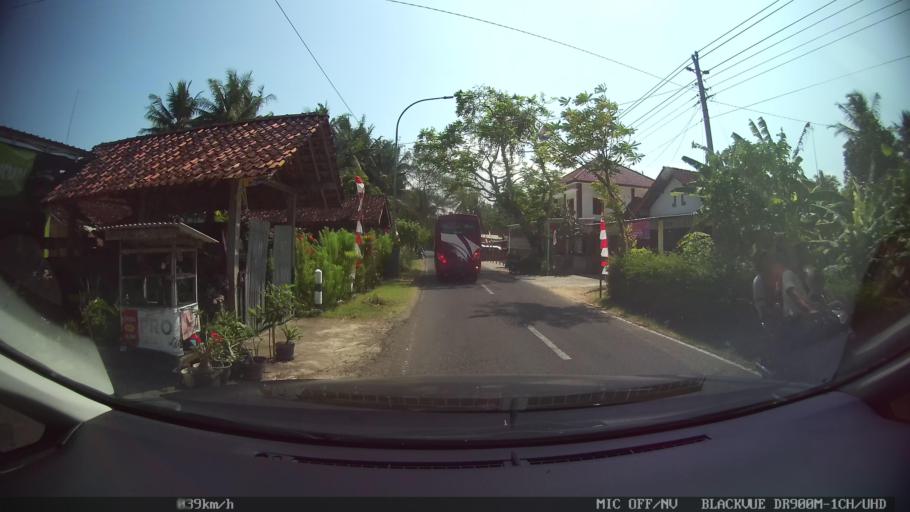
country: ID
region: Daerah Istimewa Yogyakarta
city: Srandakan
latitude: -7.9245
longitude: 110.1570
